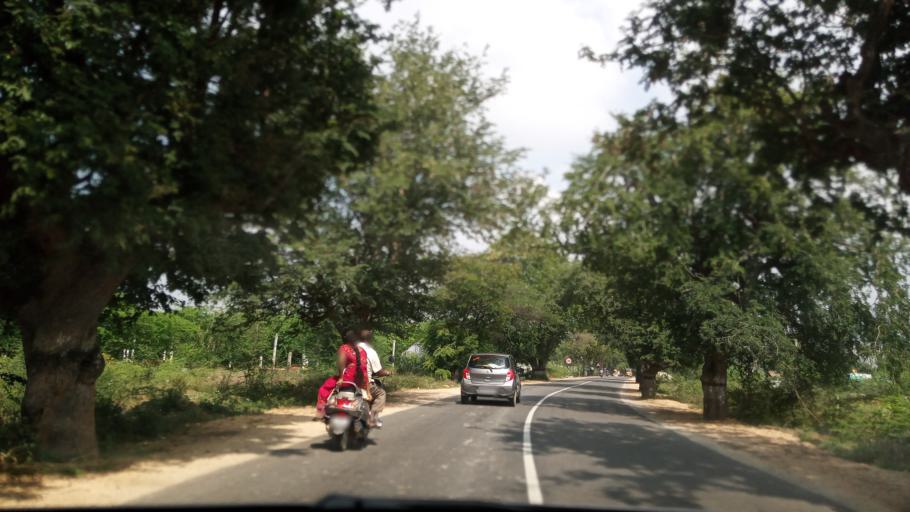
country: IN
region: Andhra Pradesh
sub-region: Chittoor
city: Madanapalle
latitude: 13.6285
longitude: 78.5507
